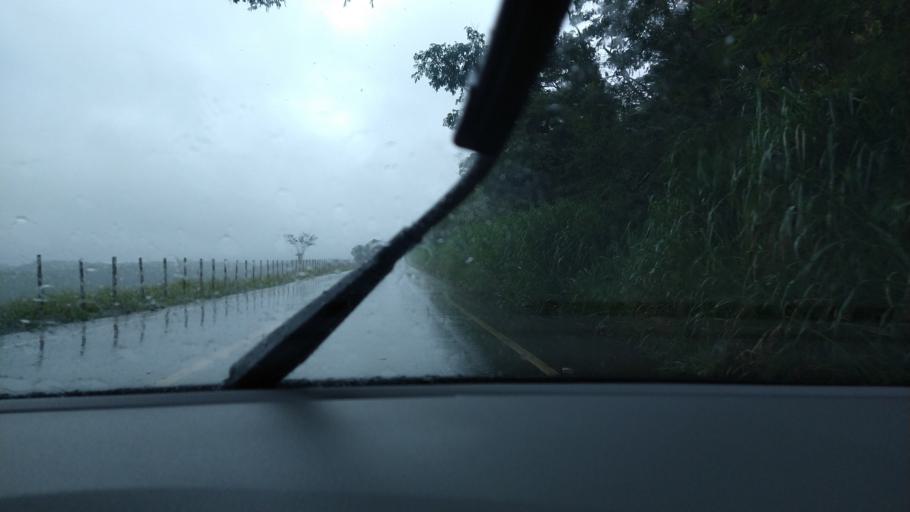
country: BR
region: Minas Gerais
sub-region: Ponte Nova
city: Ponte Nova
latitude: -20.5506
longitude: -42.8808
